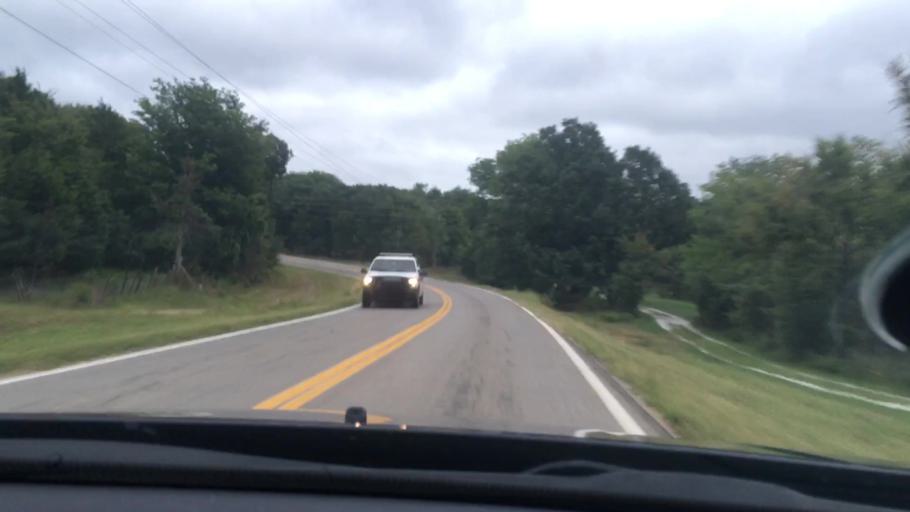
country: US
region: Oklahoma
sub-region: Sequoyah County
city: Vian
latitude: 35.6024
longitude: -95.0054
